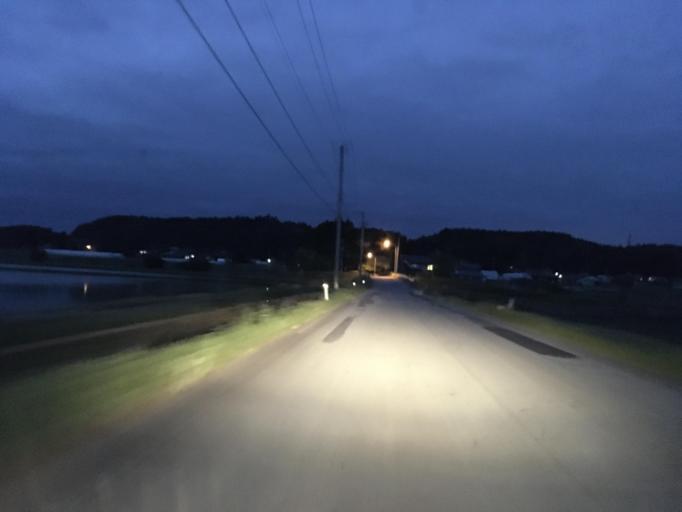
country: JP
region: Iwate
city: Ichinoseki
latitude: 38.8039
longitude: 140.9925
